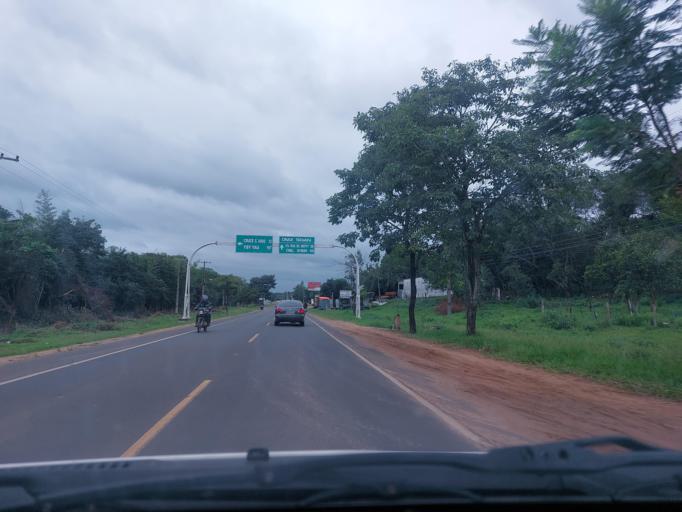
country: PY
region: San Pedro
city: Guayaybi
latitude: -24.6757
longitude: -56.4039
